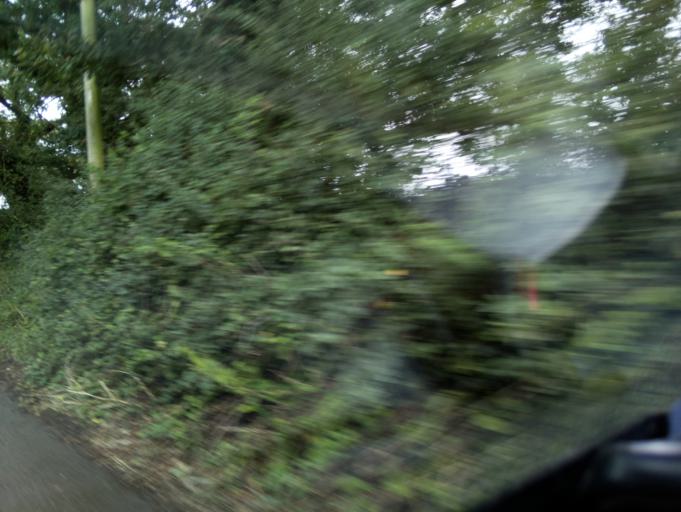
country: GB
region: England
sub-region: Devon
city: Kingsbridge
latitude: 50.2803
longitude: -3.7191
